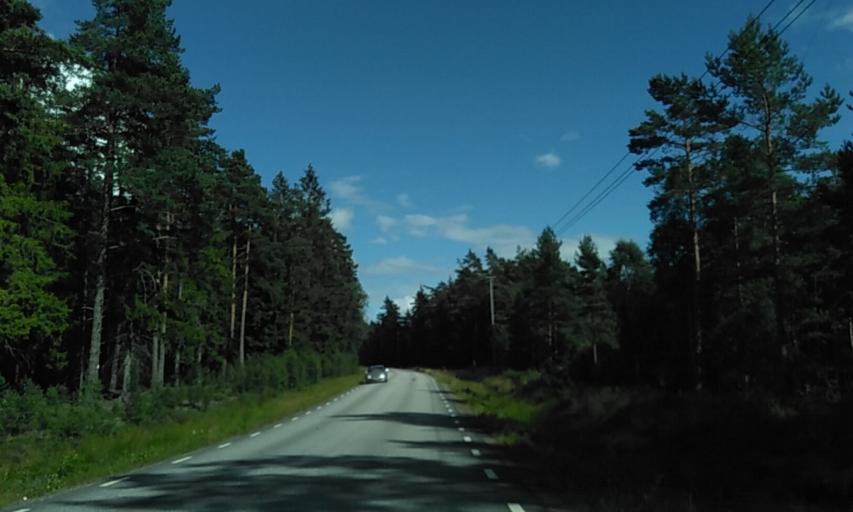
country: SE
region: Vaestra Goetaland
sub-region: Vargarda Kommun
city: Jonstorp
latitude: 57.9377
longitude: 12.7519
